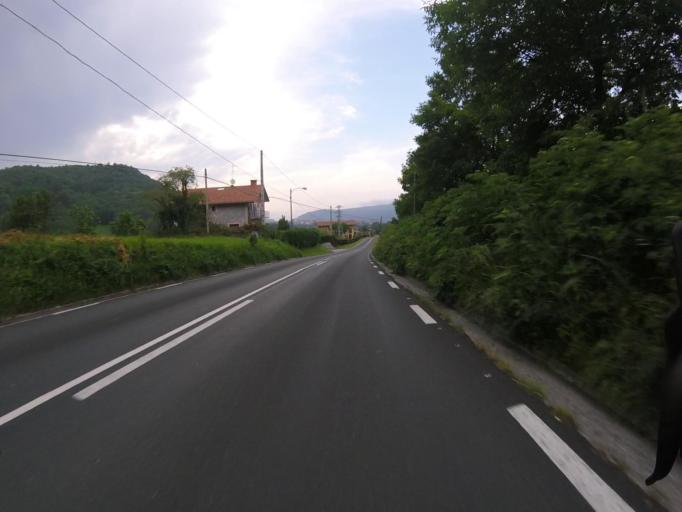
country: ES
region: Basque Country
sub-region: Provincia de Guipuzcoa
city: Errenteria
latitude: 43.2931
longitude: -1.9047
